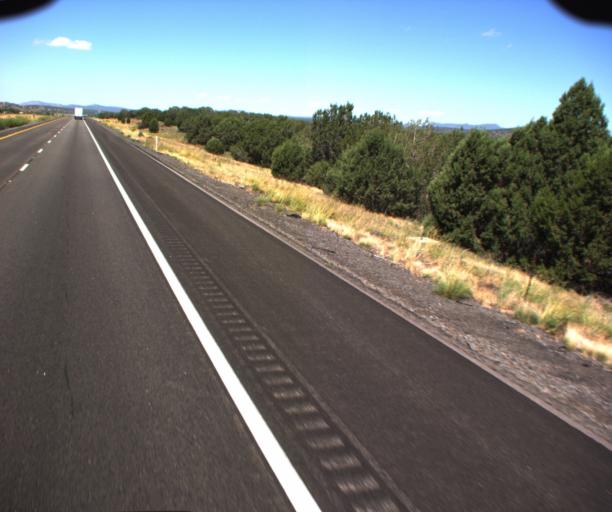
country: US
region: Arizona
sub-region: Mohave County
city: Peach Springs
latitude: 35.1912
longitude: -113.3444
